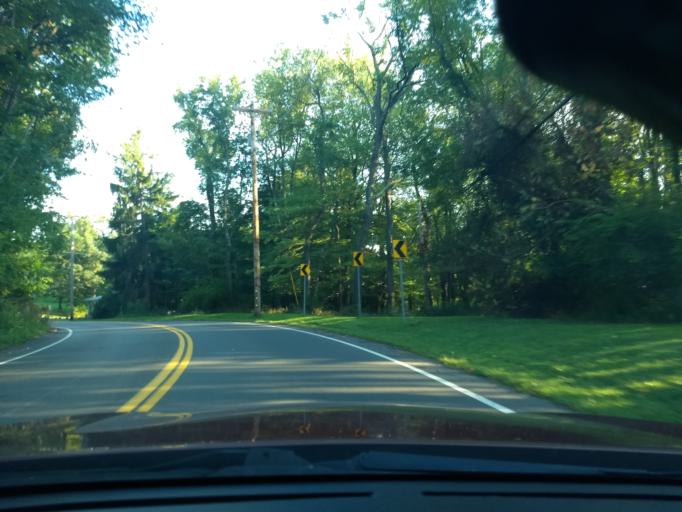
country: US
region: Pennsylvania
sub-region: Allegheny County
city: Gibsonia
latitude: 40.6405
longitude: -79.9549
